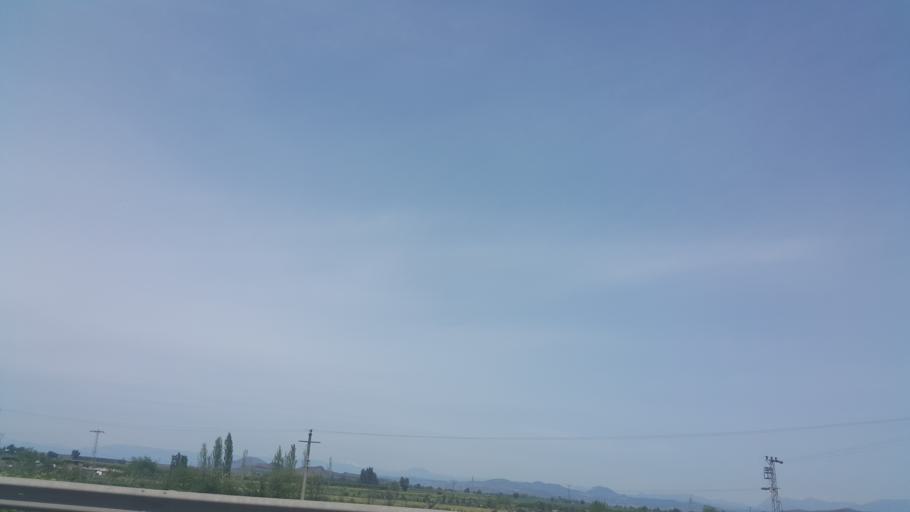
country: TR
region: Osmaniye
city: Toprakkale
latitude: 37.0751
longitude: 36.0818
